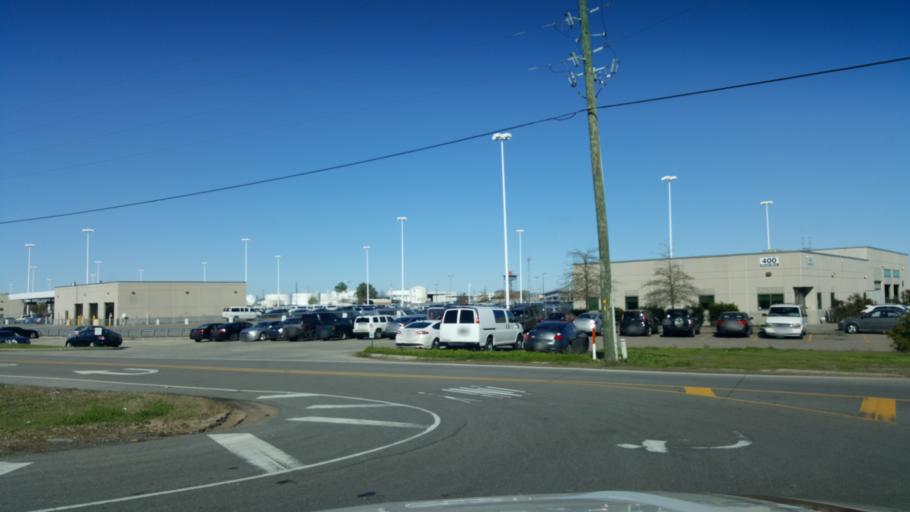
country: US
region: Louisiana
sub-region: Jefferson Parish
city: Kenner
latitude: 29.9836
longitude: -90.2635
